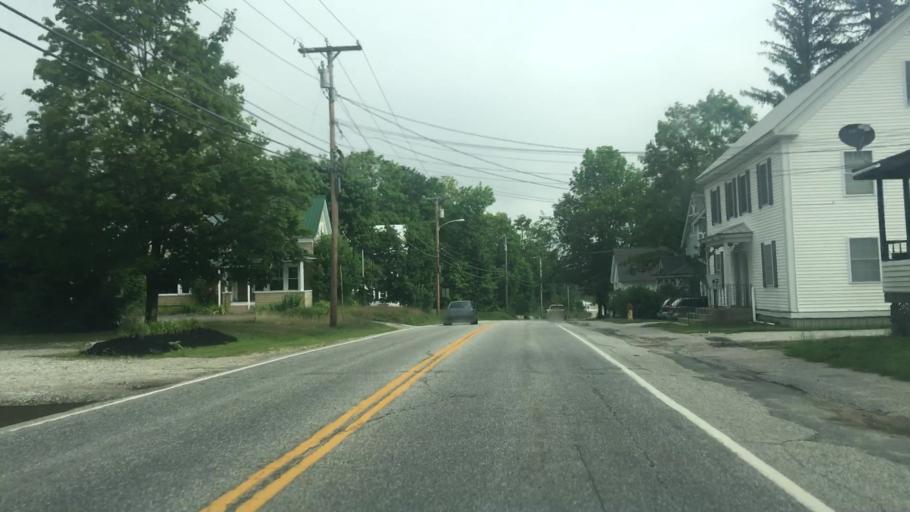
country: US
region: Maine
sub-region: Oxford County
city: South Paris
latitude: 44.2268
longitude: -70.5141
